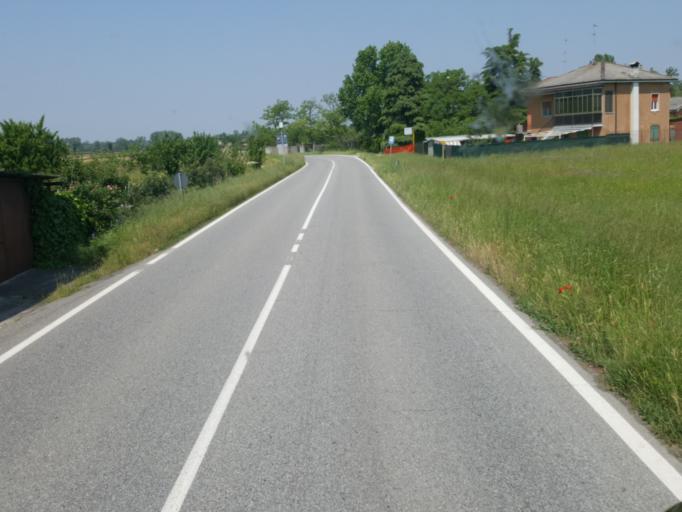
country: IT
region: Lombardy
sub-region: Provincia di Lodi
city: Lodi
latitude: 45.3296
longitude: 9.5089
